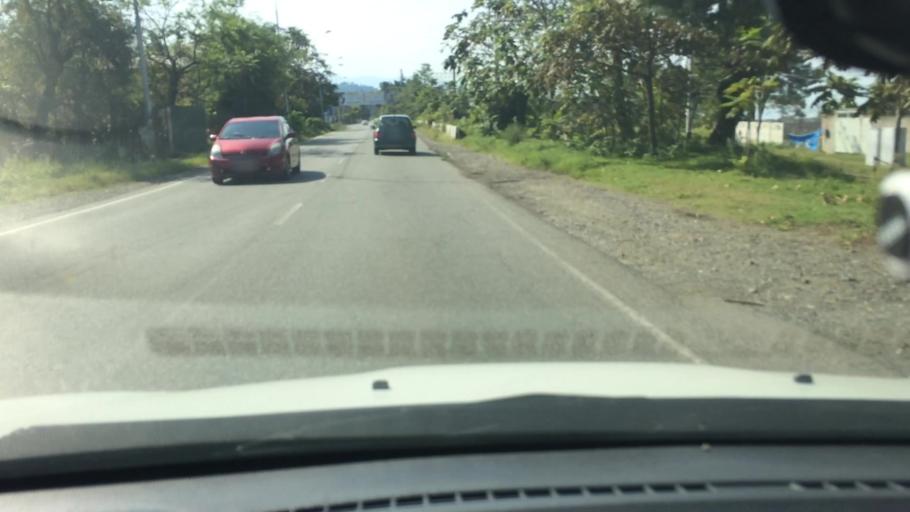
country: GE
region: Ajaria
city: Makhinjauri
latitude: 41.7373
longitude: 41.7348
